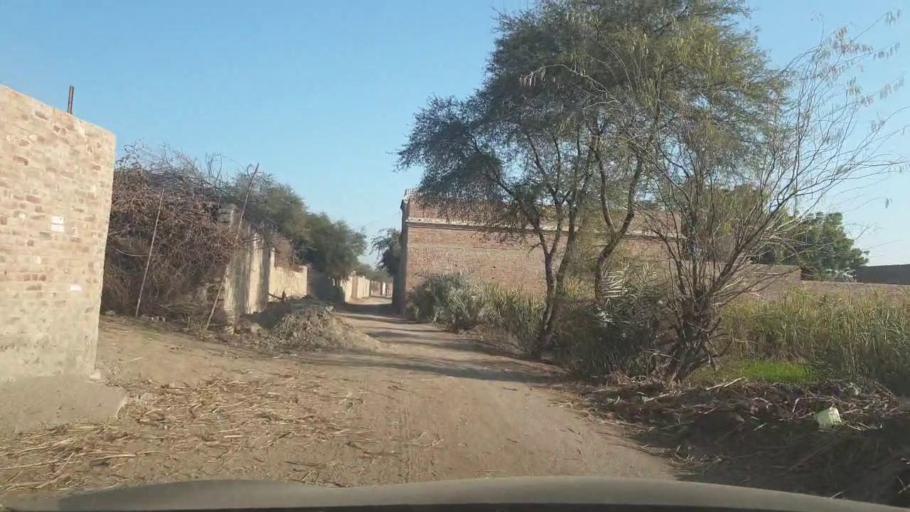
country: PK
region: Sindh
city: Ghotki
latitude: 28.0694
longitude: 69.3653
